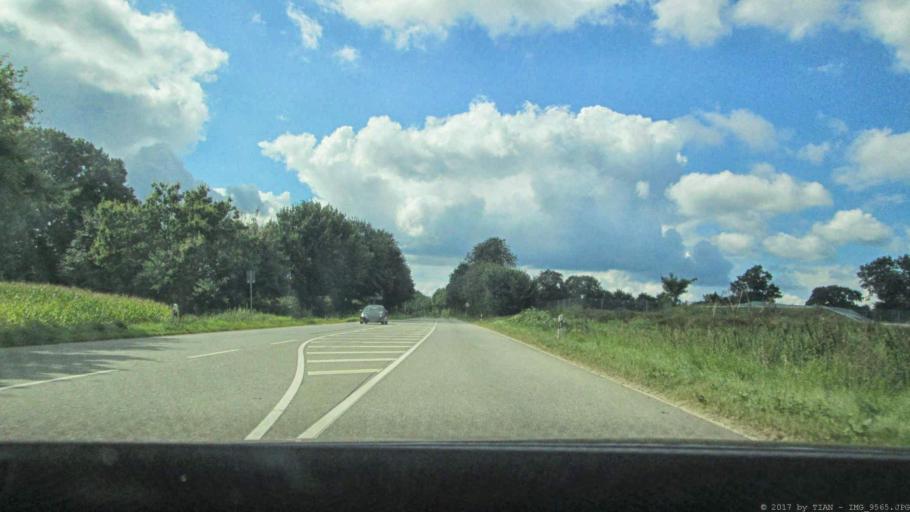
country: DE
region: Schleswig-Holstein
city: Itzstedt
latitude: 53.8167
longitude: 10.1723
